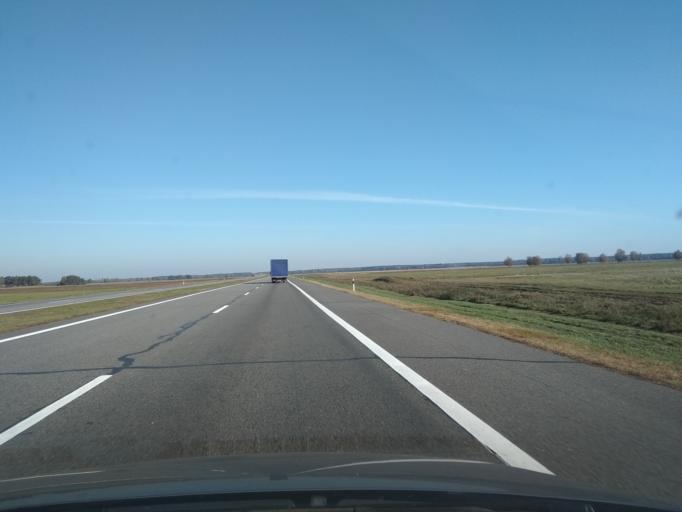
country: BY
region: Brest
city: Ivatsevichy
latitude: 52.7255
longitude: 25.4403
